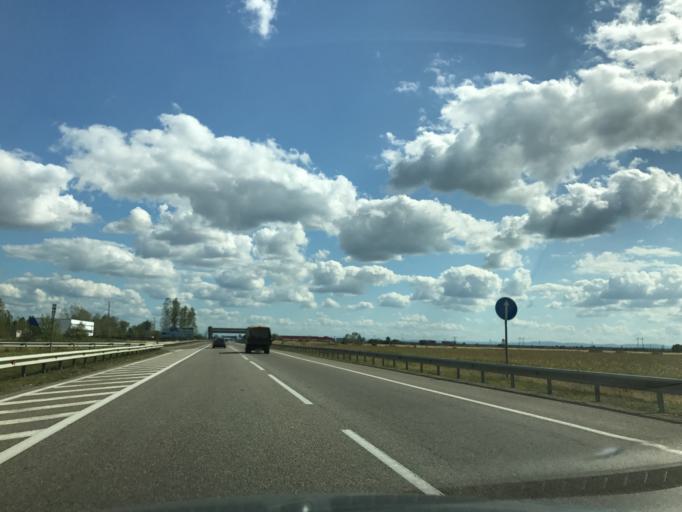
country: RU
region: Adygeya
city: Adygeysk
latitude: 44.8857
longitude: 39.1736
